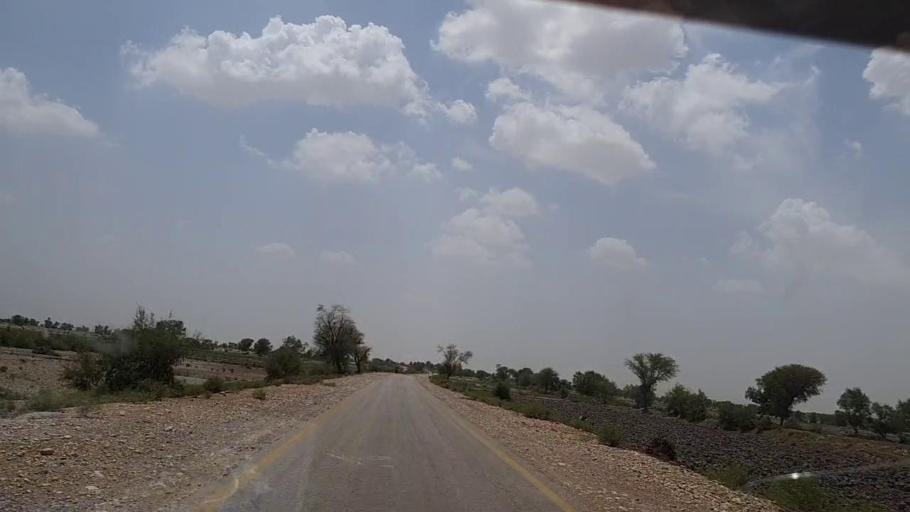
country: PK
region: Sindh
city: Bhan
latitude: 26.5415
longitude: 67.6432
